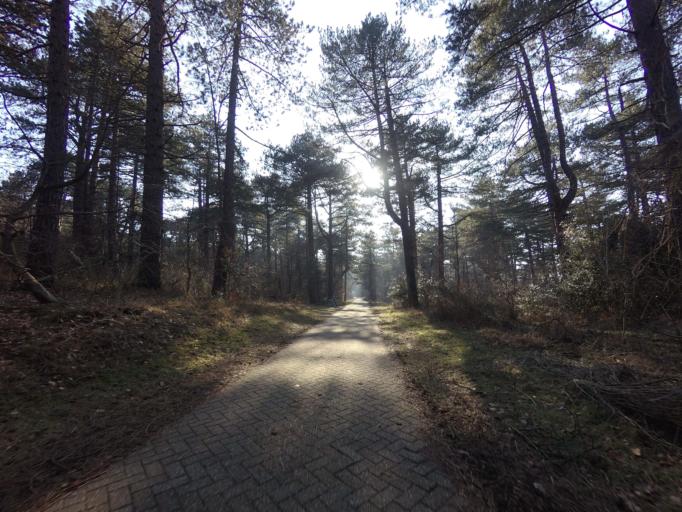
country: NL
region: North Holland
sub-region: Gemeente Bloemendaal
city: Bloemendaal
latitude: 52.4087
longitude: 4.6019
